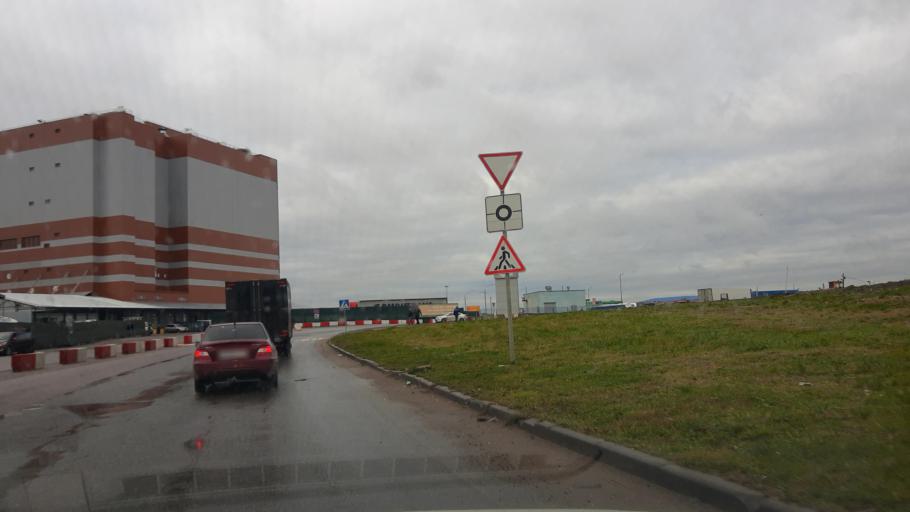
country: RU
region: Moskovskaya
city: Mosrentgen
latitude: 55.6010
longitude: 37.4637
